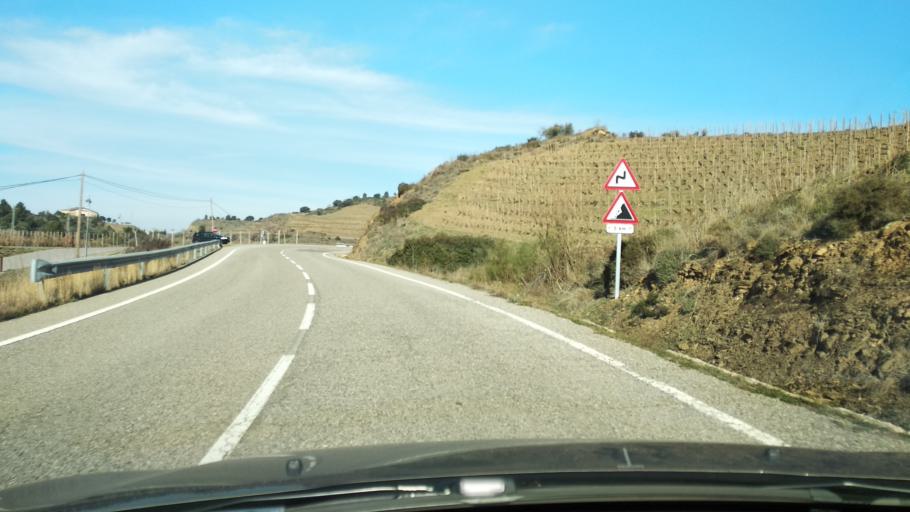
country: ES
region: Catalonia
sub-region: Provincia de Tarragona
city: Falset
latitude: 41.2008
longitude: 0.7818
